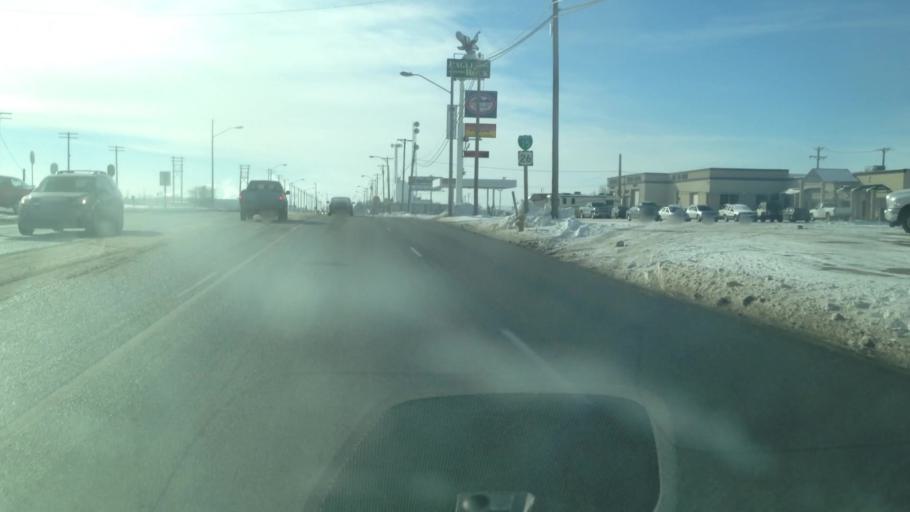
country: US
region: Idaho
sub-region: Bonneville County
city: Idaho Falls
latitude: 43.4816
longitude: -112.0462
